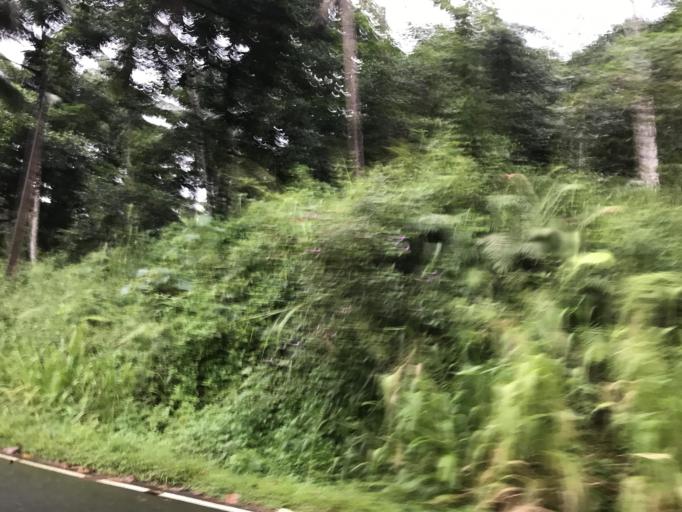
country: LK
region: Sabaragamuwa
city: Ratnapura
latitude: 6.5395
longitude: 80.2970
